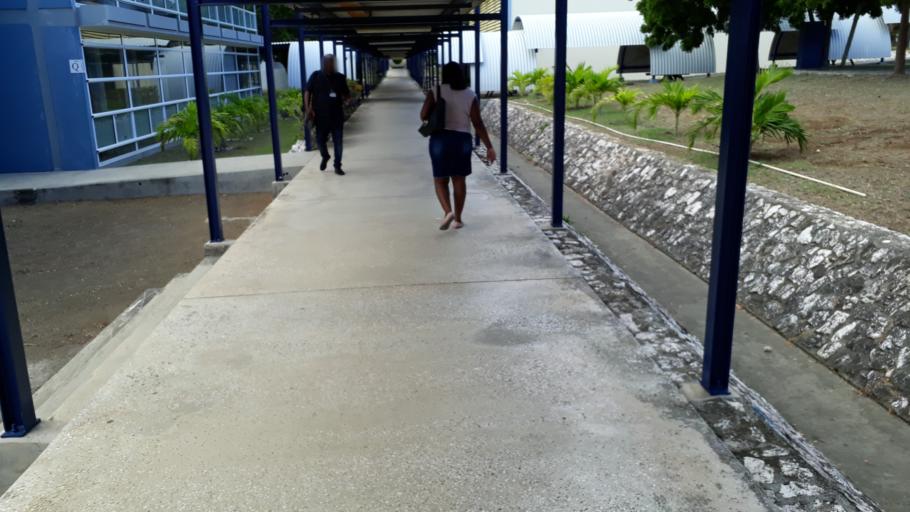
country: CW
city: Sint Michiel Liber
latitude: 12.1570
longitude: -68.9611
